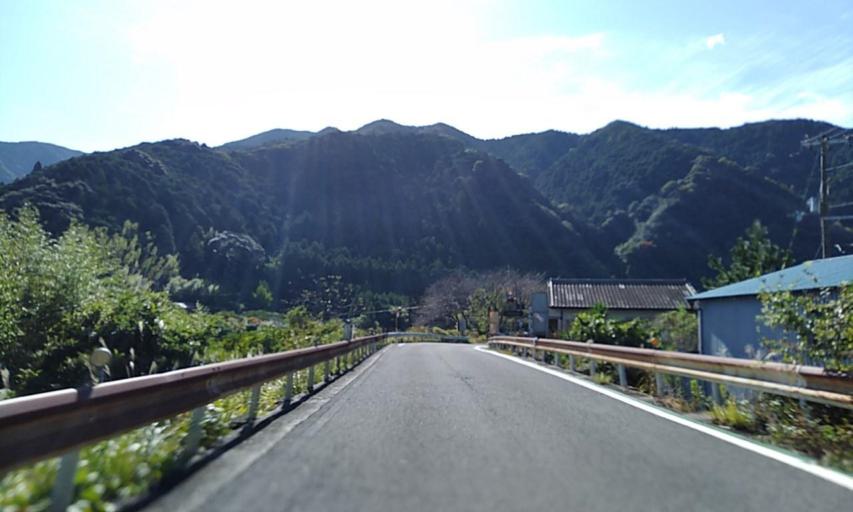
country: JP
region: Wakayama
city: Kainan
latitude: 34.0494
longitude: 135.3147
